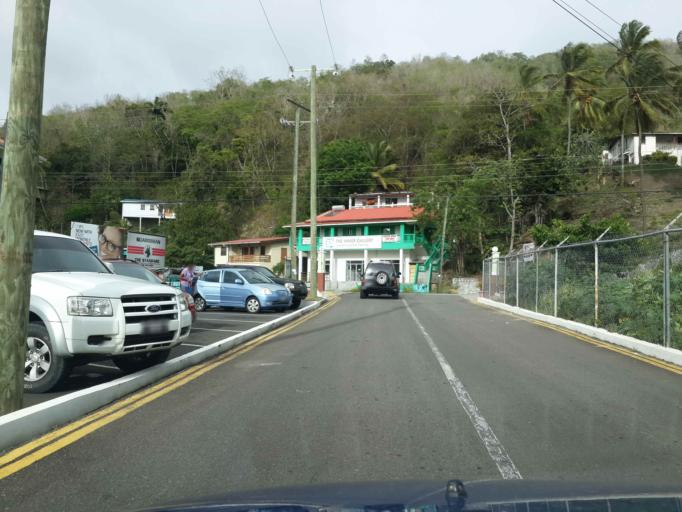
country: LC
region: Gros-Islet
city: Gros Islet
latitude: 14.0571
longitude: -60.9593
